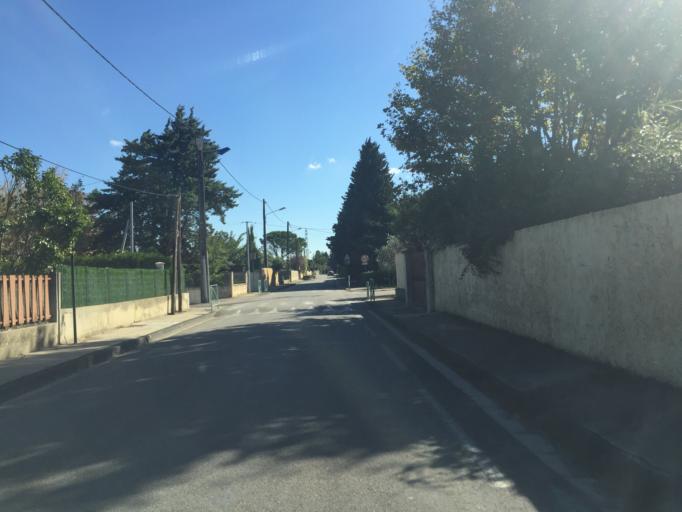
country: FR
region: Provence-Alpes-Cote d'Azur
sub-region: Departement du Vaucluse
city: Vedene
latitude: 43.9743
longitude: 4.9057
